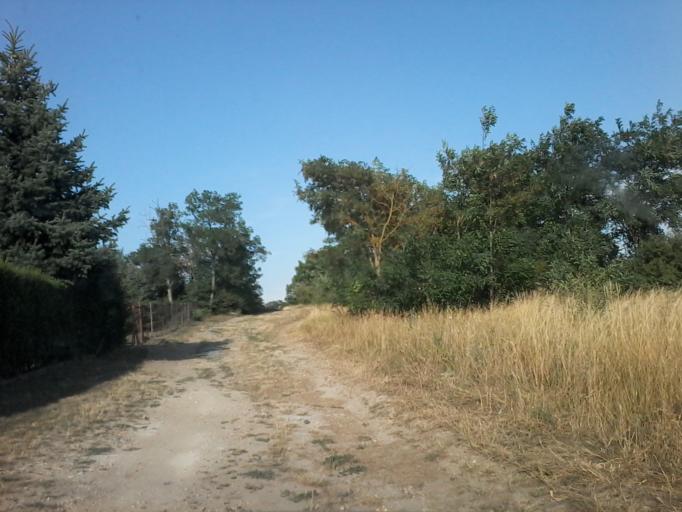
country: HU
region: Vas
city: Sarvar
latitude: 47.2171
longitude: 17.0051
